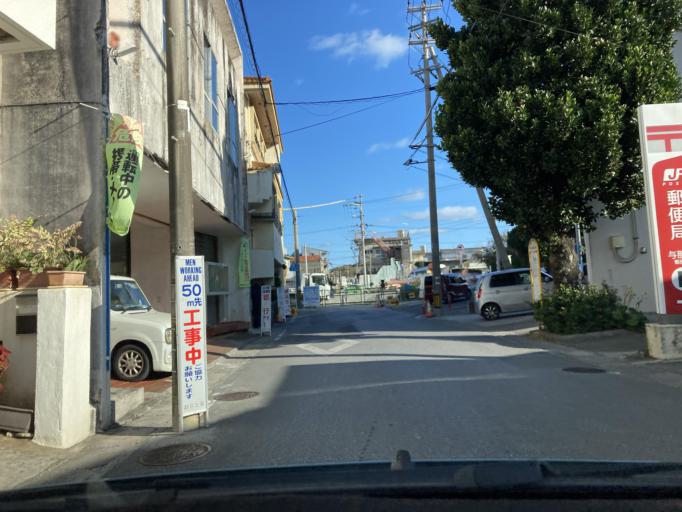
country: JP
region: Okinawa
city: Katsuren-haebaru
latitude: 26.3231
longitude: 127.9082
